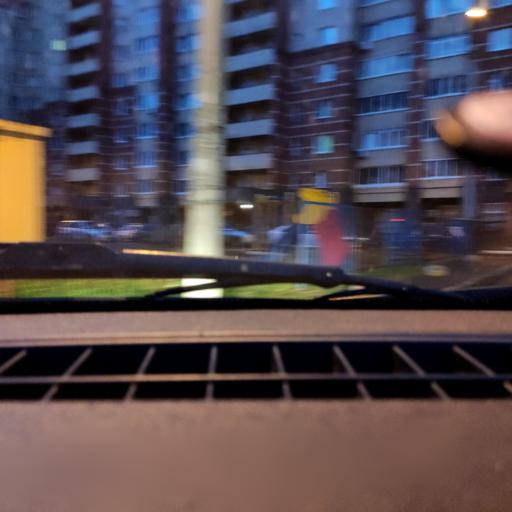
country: RU
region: Bashkortostan
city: Ufa
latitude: 54.7811
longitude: 56.1225
